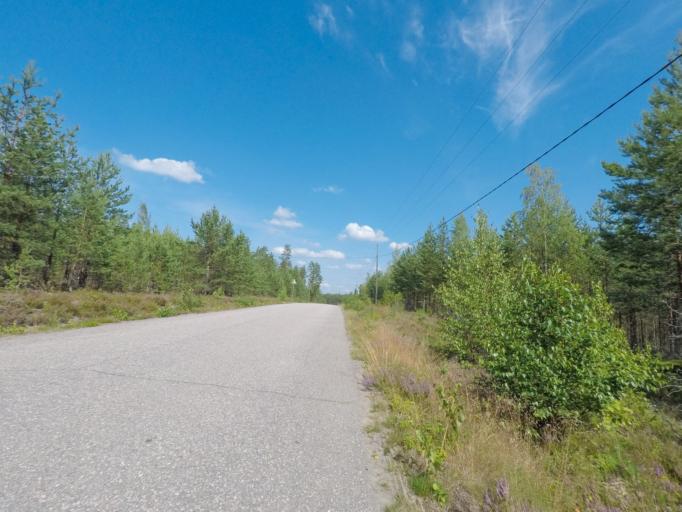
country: FI
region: Southern Savonia
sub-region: Mikkeli
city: Puumala
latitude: 61.4284
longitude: 28.1645
